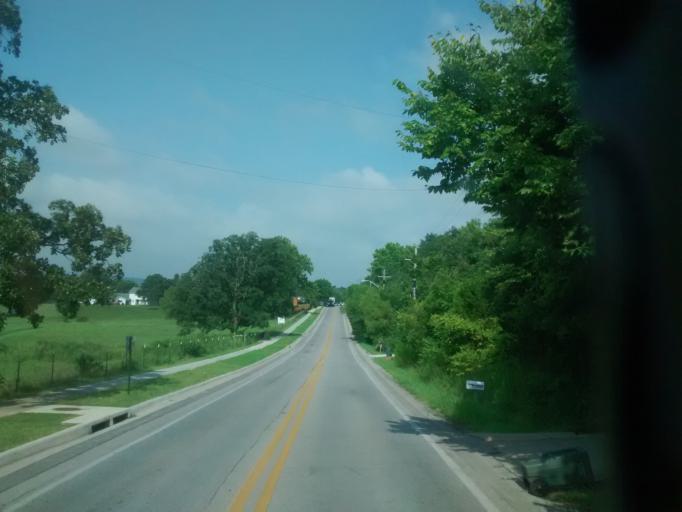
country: US
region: Arkansas
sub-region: Washington County
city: Fayetteville
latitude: 36.0552
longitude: -94.1445
